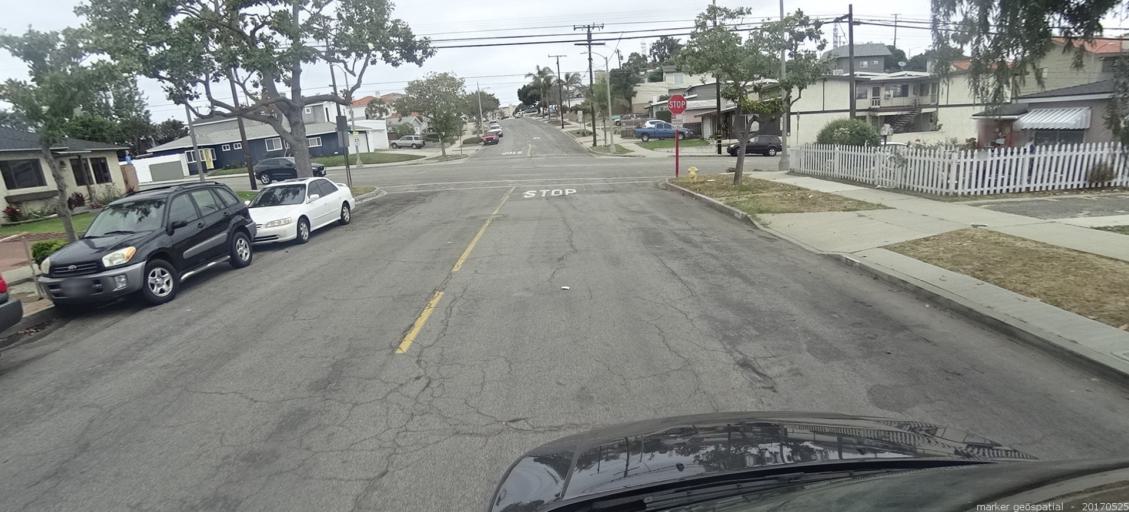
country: US
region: California
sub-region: Los Angeles County
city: Redondo Beach
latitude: 33.8533
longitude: -118.3826
